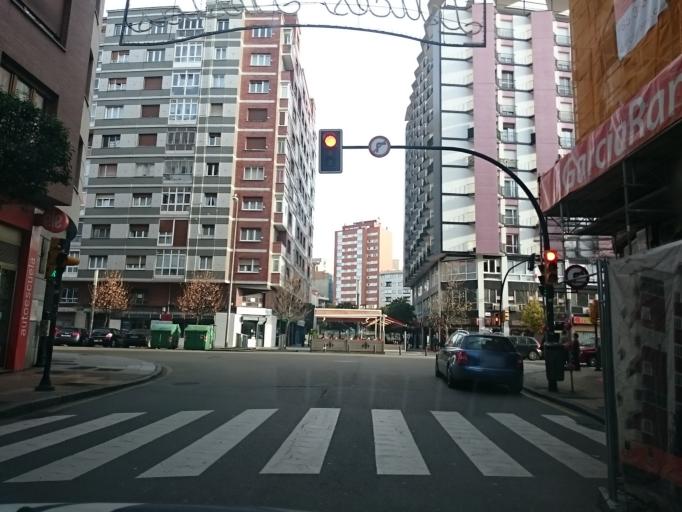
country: ES
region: Asturias
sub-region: Province of Asturias
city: Gijon
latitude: 43.5413
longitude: -5.6569
